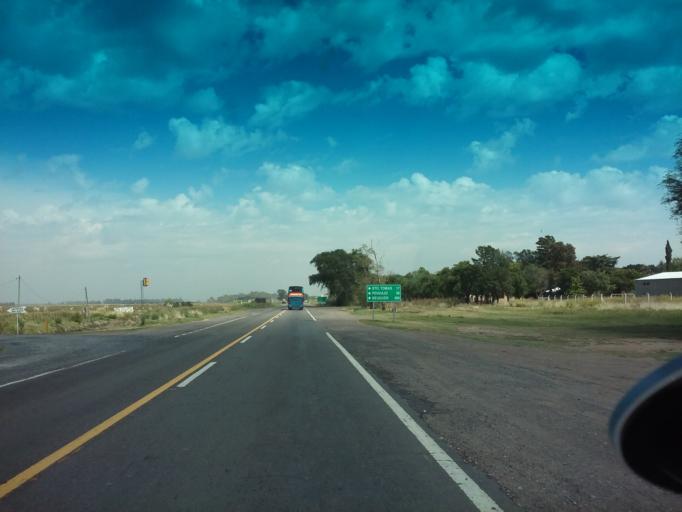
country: AR
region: Buenos Aires
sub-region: Partido de Carlos Casares
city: Carlos Casares
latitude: -35.6401
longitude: -61.3610
